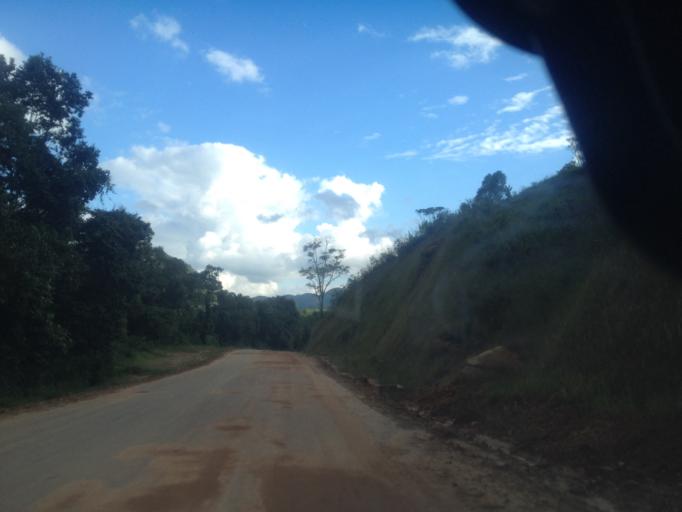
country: BR
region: Rio de Janeiro
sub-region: Quatis
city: Quatis
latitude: -22.2219
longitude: -44.2508
